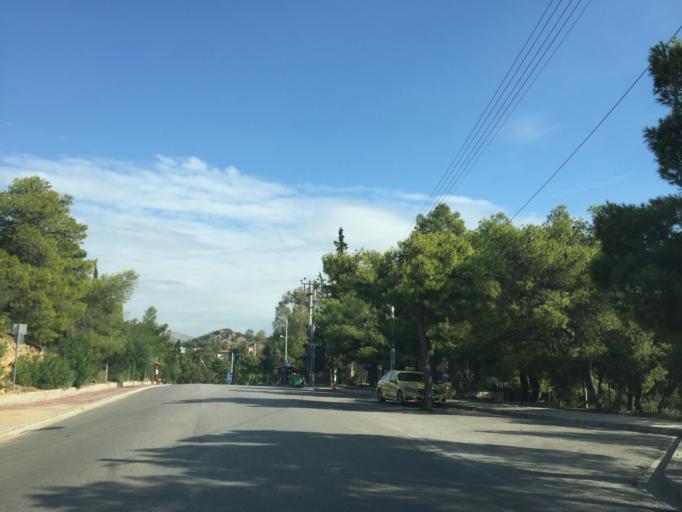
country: GR
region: Attica
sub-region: Nomarchia Anatolikis Attikis
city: Vouliagmeni
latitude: 37.8204
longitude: 23.7739
